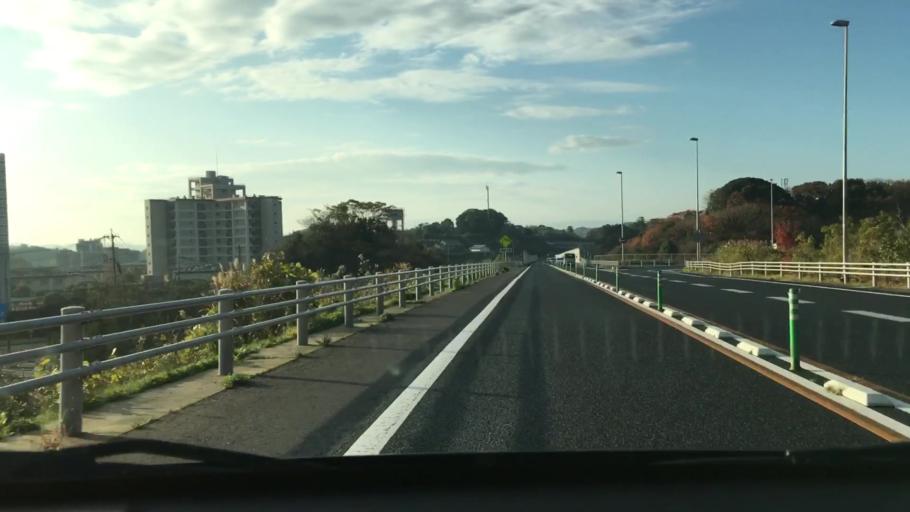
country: JP
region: Nagasaki
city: Sasebo
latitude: 33.0863
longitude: 129.7776
